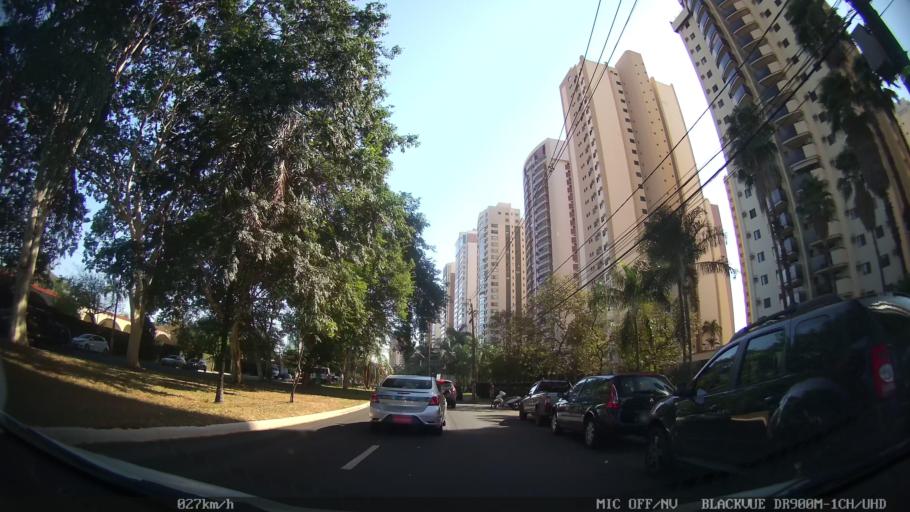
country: BR
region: Sao Paulo
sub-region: Ribeirao Preto
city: Ribeirao Preto
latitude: -21.2097
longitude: -47.8067
